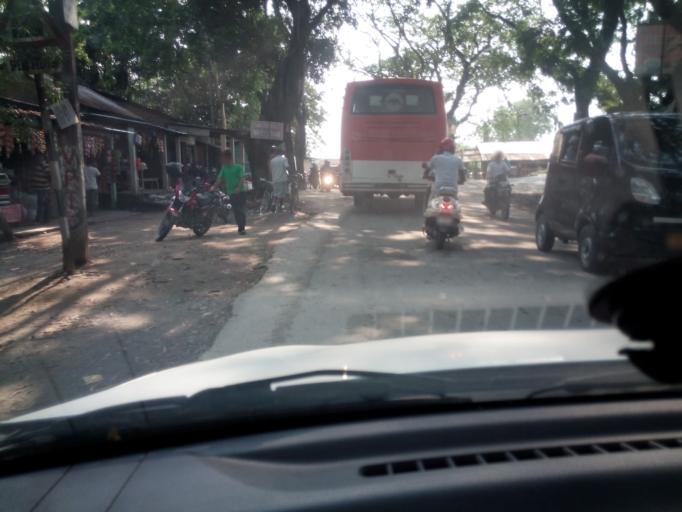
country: IN
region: Assam
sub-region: Udalguri
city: Udalguri
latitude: 26.7455
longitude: 92.1115
